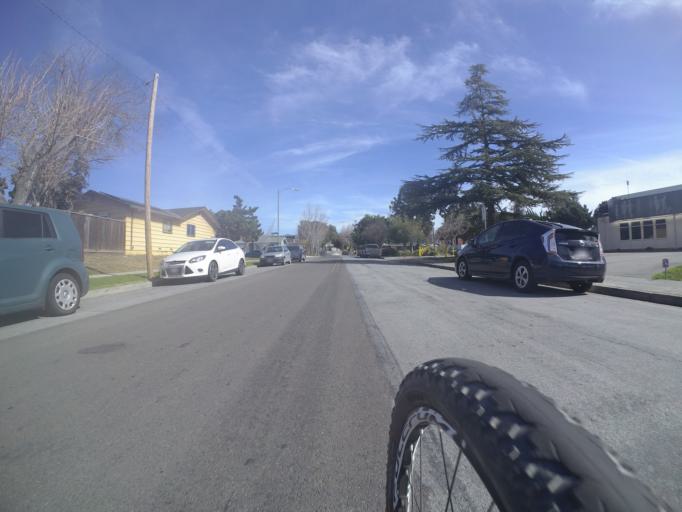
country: US
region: California
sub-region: Santa Clara County
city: Milpitas
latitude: 37.4094
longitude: -121.8816
